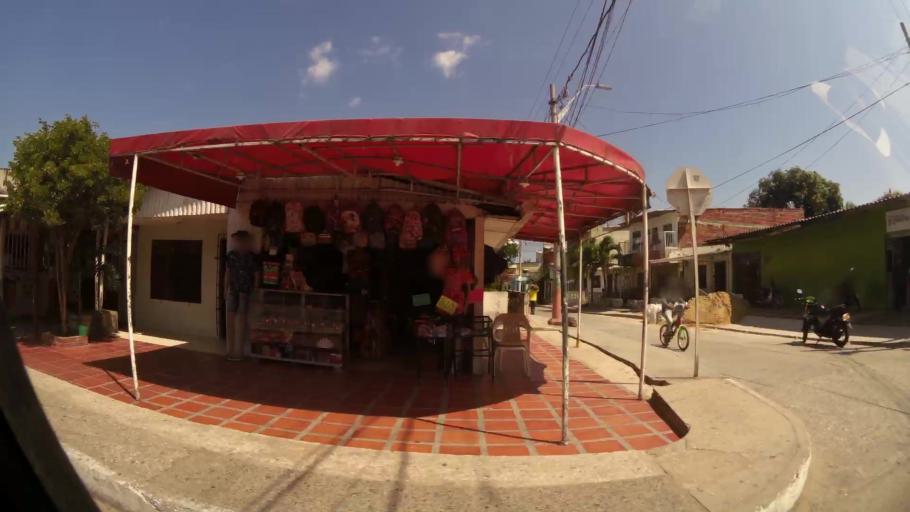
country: CO
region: Atlantico
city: Barranquilla
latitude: 10.9663
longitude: -74.8346
